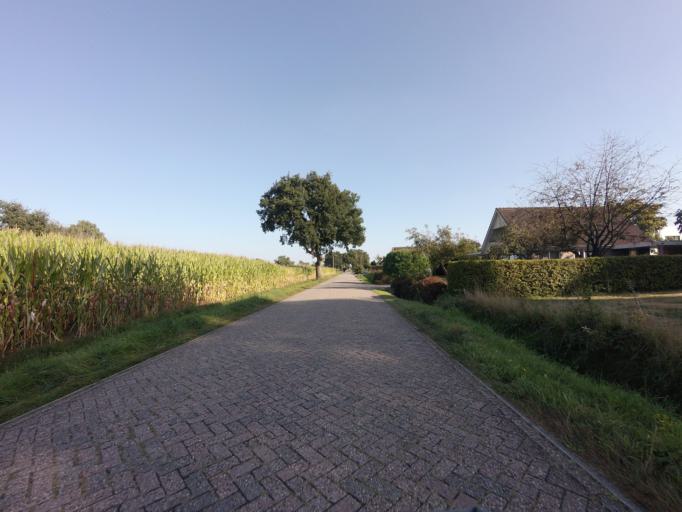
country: NL
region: Overijssel
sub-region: Gemeente Hardenberg
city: Hardenberg
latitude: 52.5613
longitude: 6.6373
